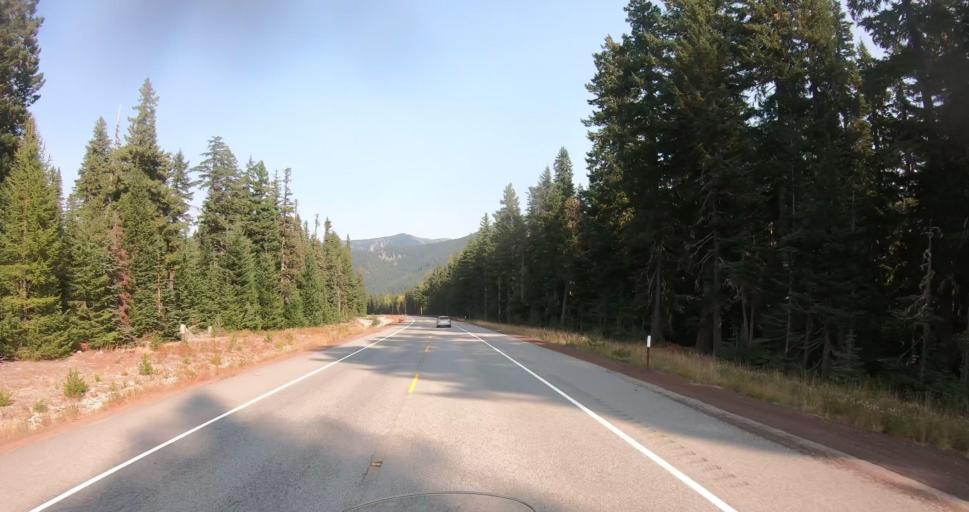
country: US
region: Oregon
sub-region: Hood River County
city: Odell
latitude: 45.3216
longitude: -121.6022
